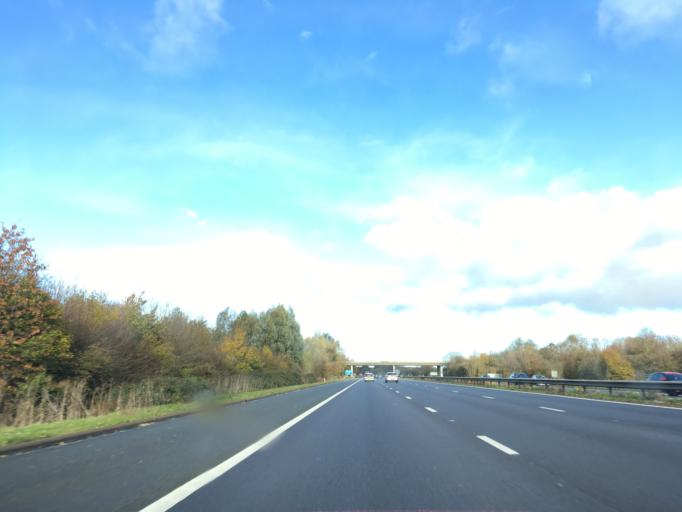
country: GB
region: England
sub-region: Worcestershire
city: Bredon
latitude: 52.0092
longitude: -2.1216
